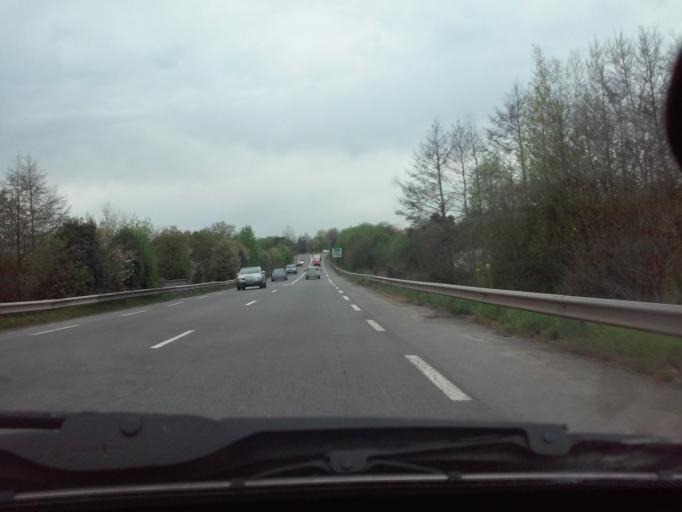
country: FR
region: Brittany
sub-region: Departement d'Ille-et-Vilaine
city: Fougeres
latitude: 48.3375
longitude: -1.2061
